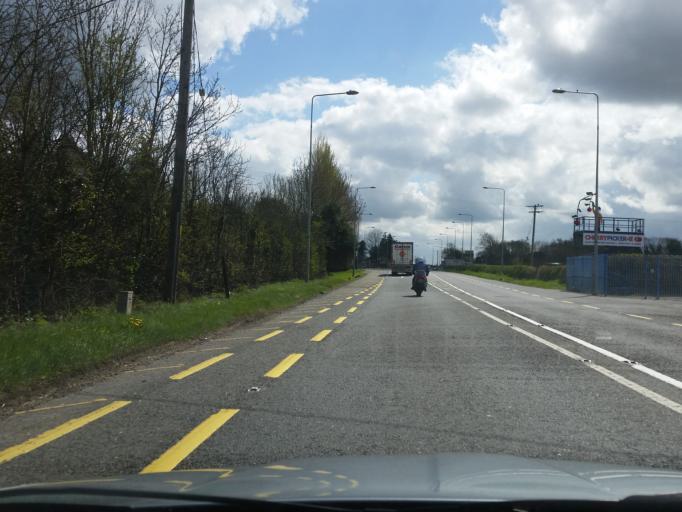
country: IE
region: Leinster
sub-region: An Mhi
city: Ratoath
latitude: 53.5737
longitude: -6.4505
